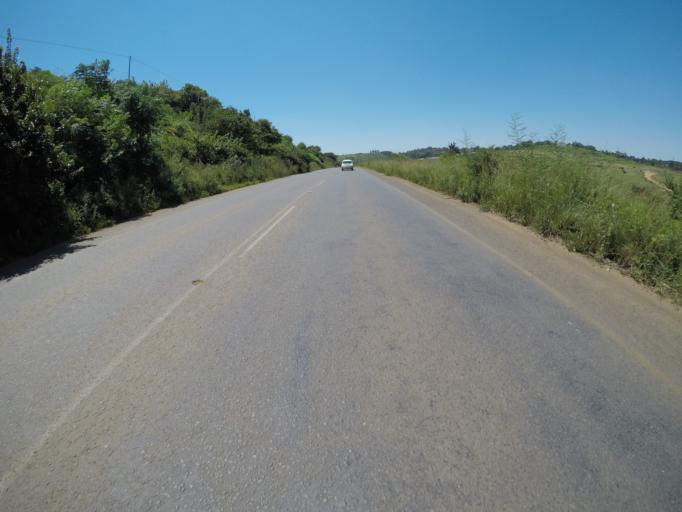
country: ZA
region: KwaZulu-Natal
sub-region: uThungulu District Municipality
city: Empangeni
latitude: -28.7548
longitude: 31.8749
